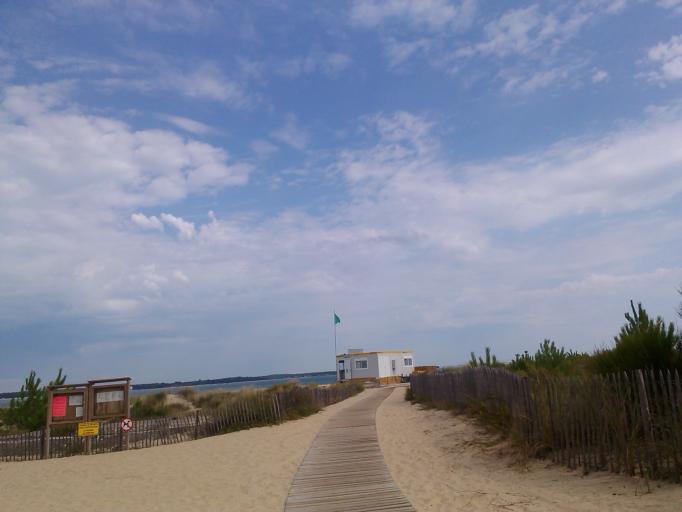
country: FR
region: Poitou-Charentes
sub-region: Departement de la Charente-Maritime
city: Saint-Trojan-les-Bains
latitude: 45.7929
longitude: -1.2068
